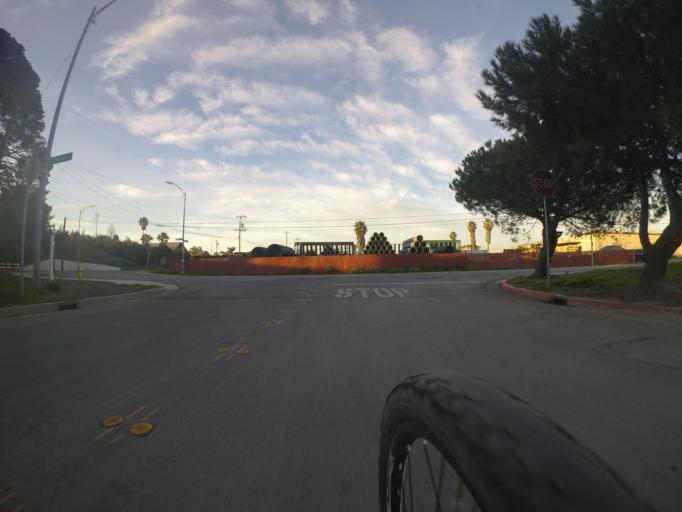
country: US
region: California
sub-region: Santa Clara County
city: Milpitas
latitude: 37.4270
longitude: -121.9786
